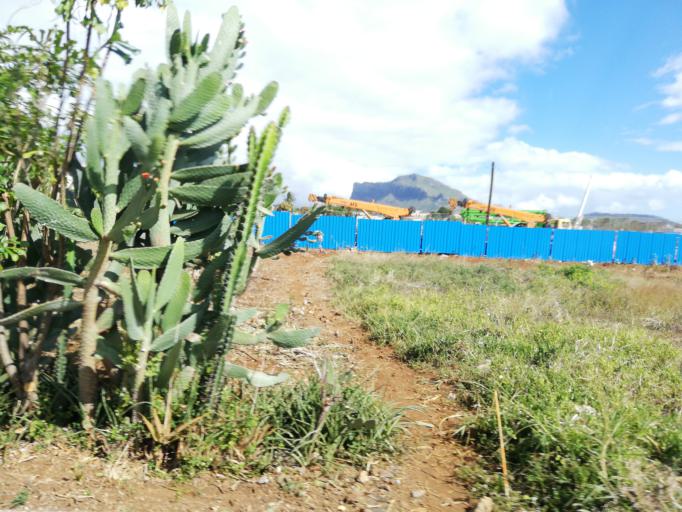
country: MU
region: Black River
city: Petite Riviere
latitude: -20.2189
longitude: 57.4602
